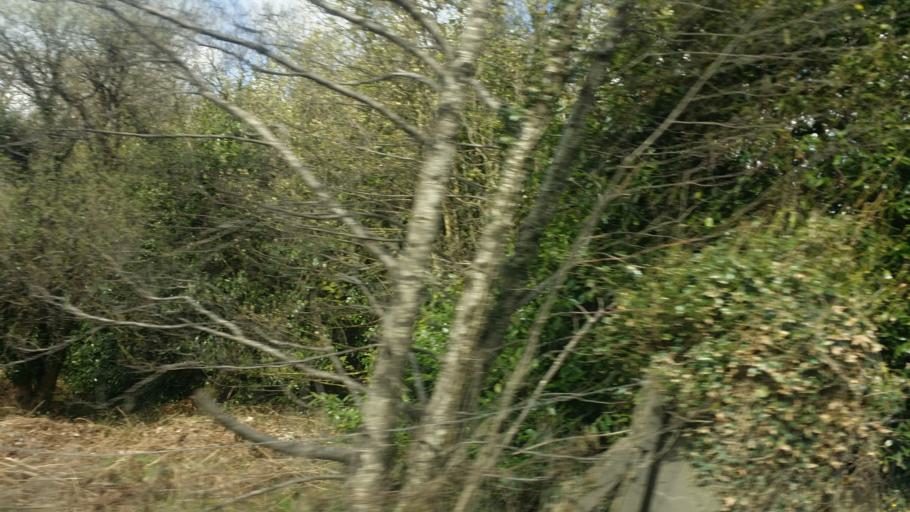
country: IE
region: Ulster
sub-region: An Cabhan
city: Ballyjamesduff
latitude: 53.9220
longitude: -7.2109
